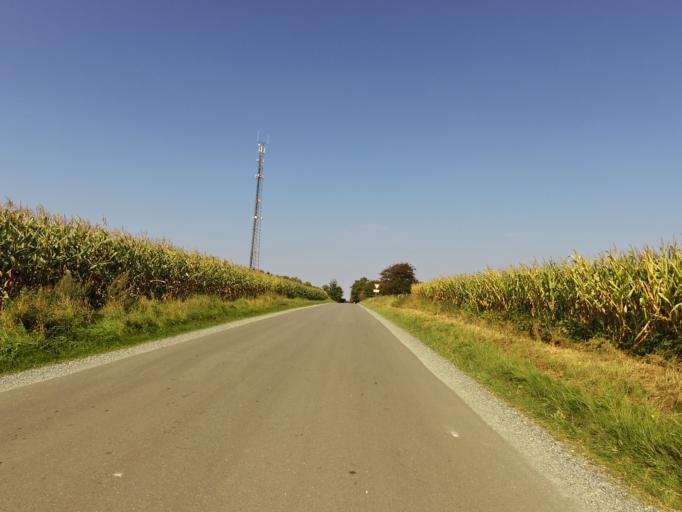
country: DK
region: South Denmark
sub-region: Vejen Kommune
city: Rodding
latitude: 55.3578
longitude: 9.1274
